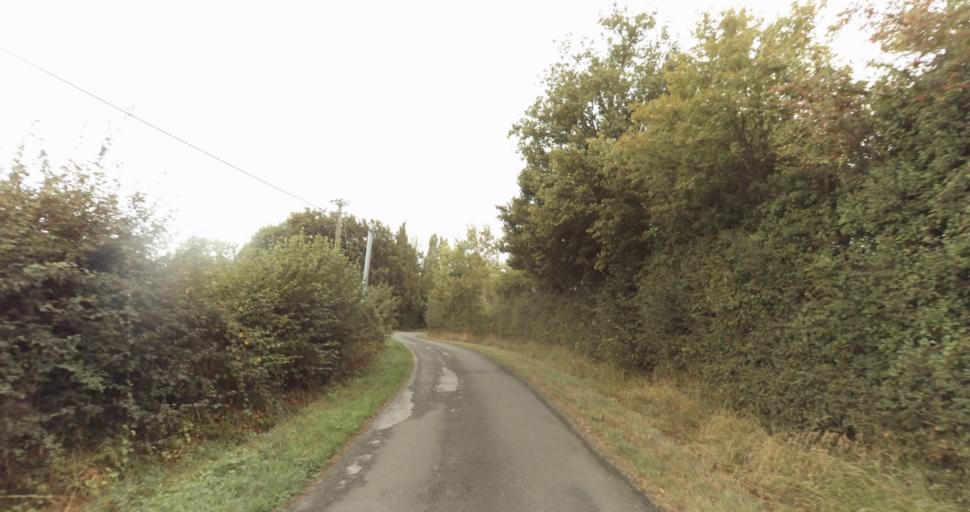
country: FR
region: Lower Normandy
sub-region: Departement de l'Orne
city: Vimoutiers
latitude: 48.8920
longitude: 0.2601
